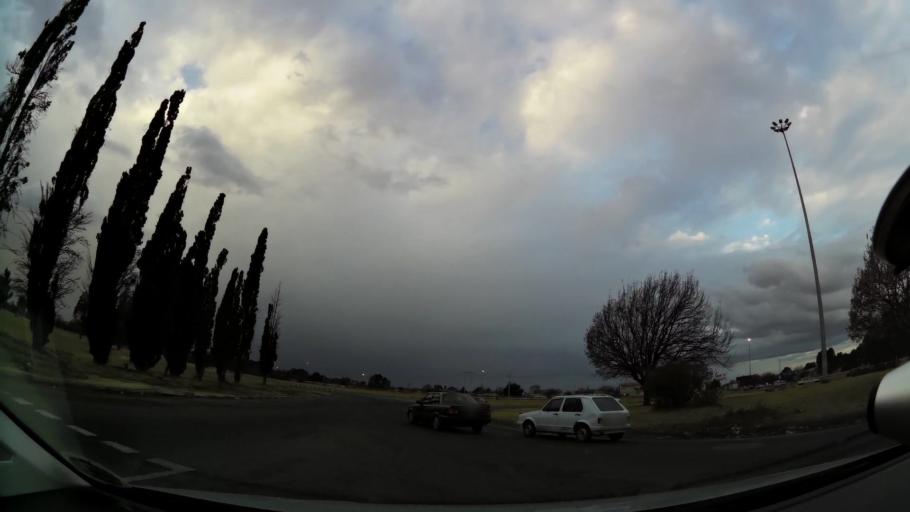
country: ZA
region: Orange Free State
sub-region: Lejweleputswa District Municipality
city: Welkom
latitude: -27.9752
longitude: 26.7741
